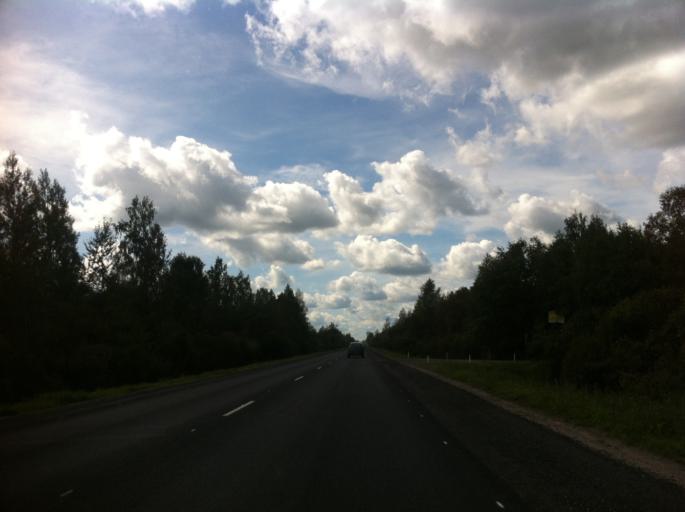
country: RU
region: Pskov
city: Izborsk
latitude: 57.7515
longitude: 28.0536
